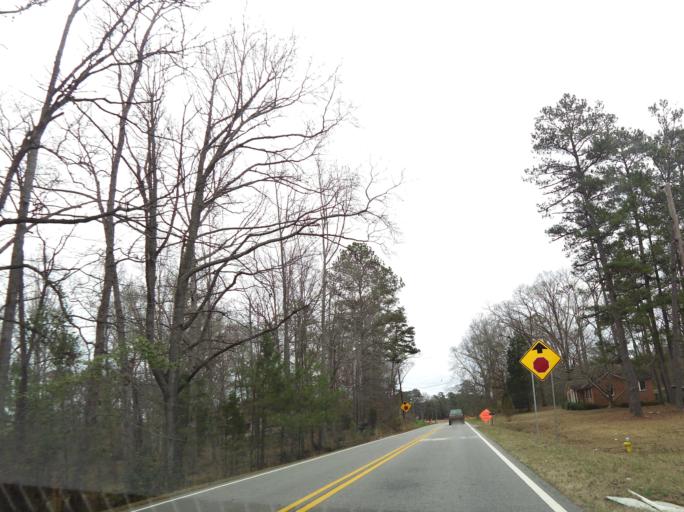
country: US
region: Georgia
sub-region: Bibb County
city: West Point
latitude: 32.8509
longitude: -83.7883
